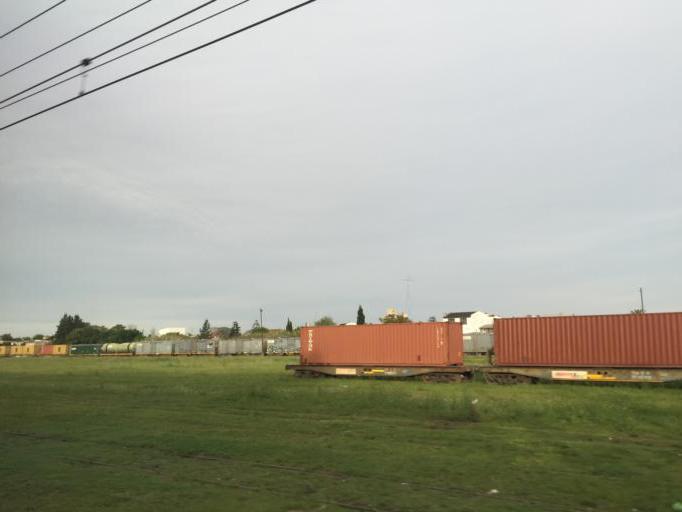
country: AR
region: Buenos Aires
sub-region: Partido de Lanus
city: Lanus
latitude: -34.6867
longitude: -58.3829
